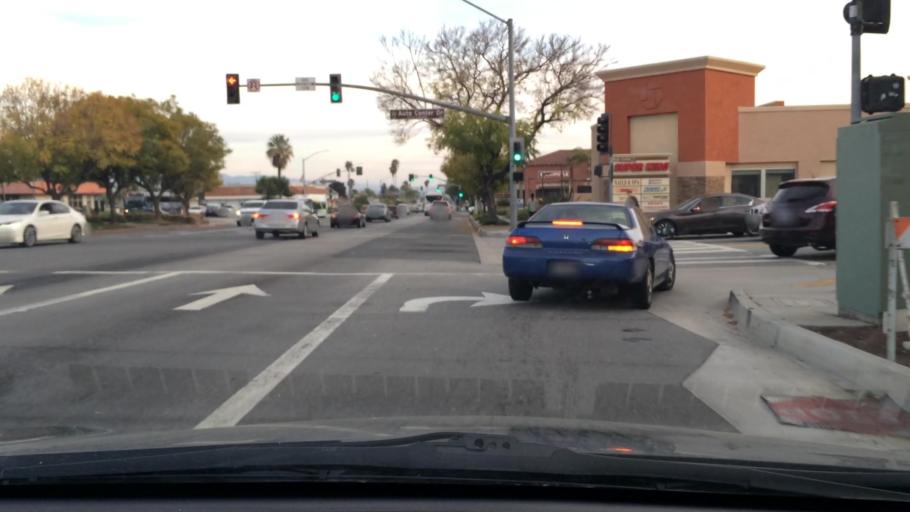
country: US
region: California
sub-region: Los Angeles County
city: Claremont
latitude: 34.0809
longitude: -117.7194
